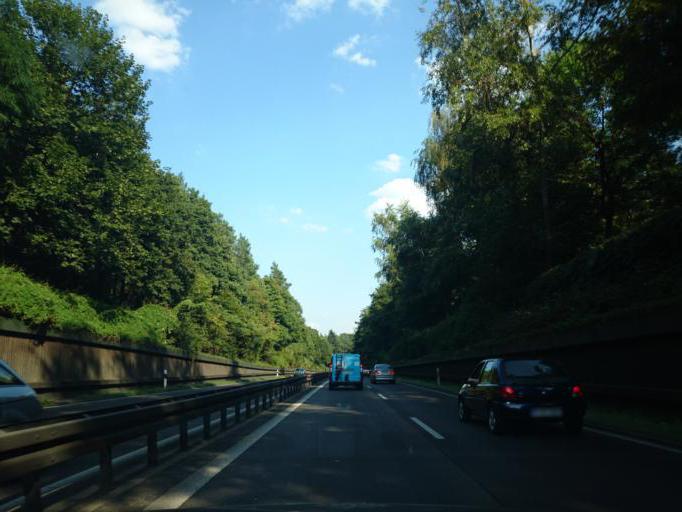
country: DE
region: Berlin
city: Heiligensee
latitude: 52.6071
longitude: 13.2643
